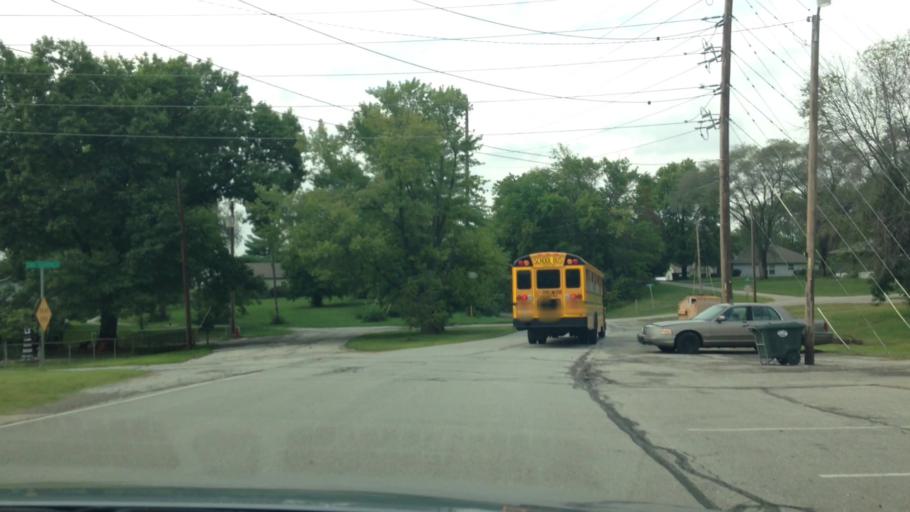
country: US
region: Missouri
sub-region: Platte County
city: Weatherby Lake
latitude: 39.3122
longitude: -94.6666
